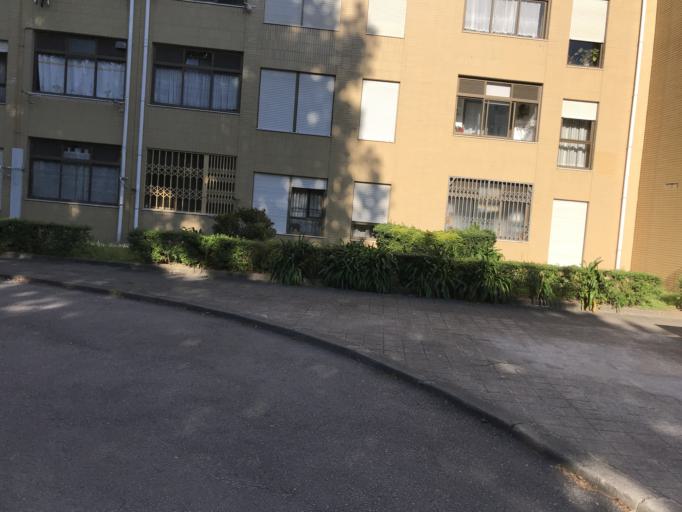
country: PT
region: Porto
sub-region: Matosinhos
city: Matosinhos
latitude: 41.1824
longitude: -8.6746
